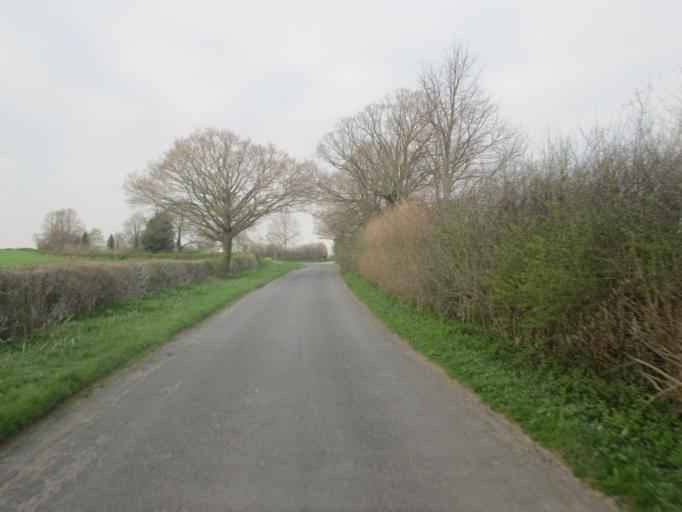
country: GB
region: England
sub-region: Derbyshire
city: Etwall
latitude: 52.9494
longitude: -1.5704
